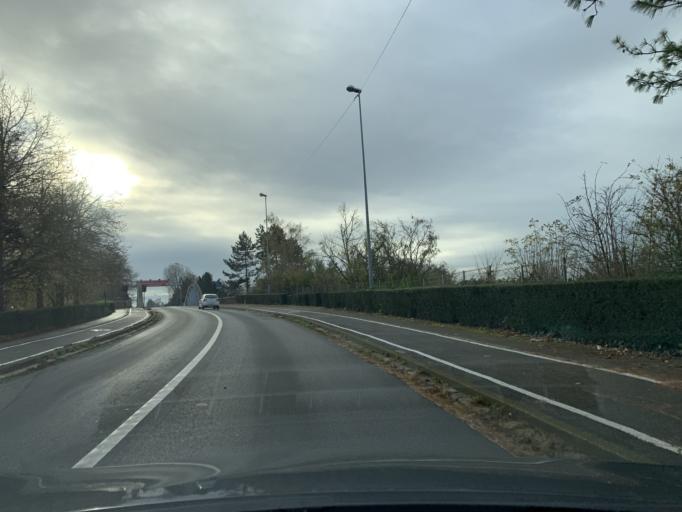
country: FR
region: Nord-Pas-de-Calais
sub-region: Departement du Nord
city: Lambres-lez-Douai
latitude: 50.3567
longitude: 3.0814
